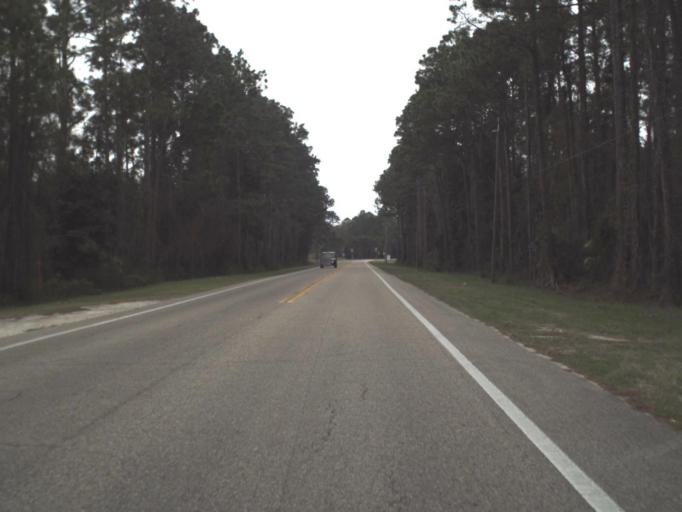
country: US
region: Florida
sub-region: Gulf County
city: Port Saint Joe
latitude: 29.8219
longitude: -85.2823
